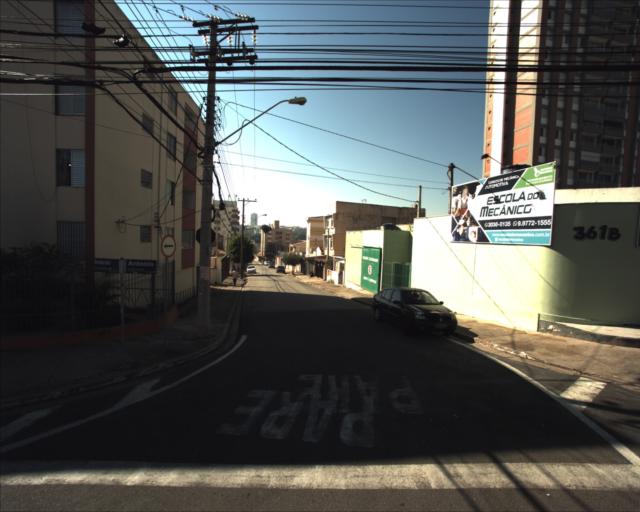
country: BR
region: Sao Paulo
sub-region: Sorocaba
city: Sorocaba
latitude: -23.5090
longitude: -47.4557
